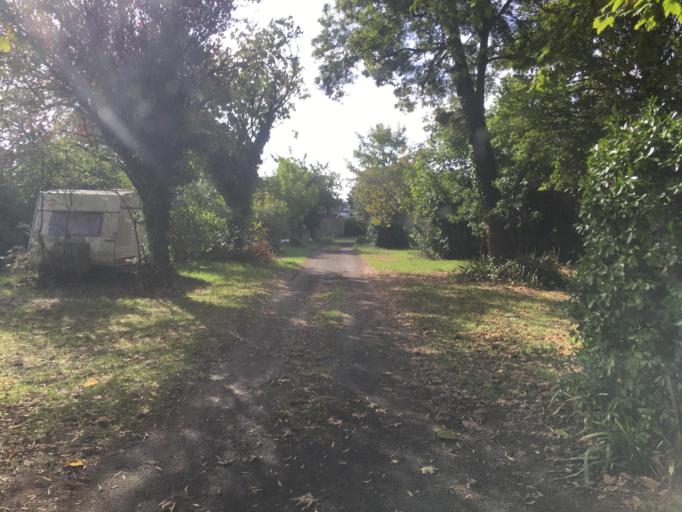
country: FR
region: Brittany
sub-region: Departement du Finistere
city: Loctudy
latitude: 47.8099
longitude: -4.1764
